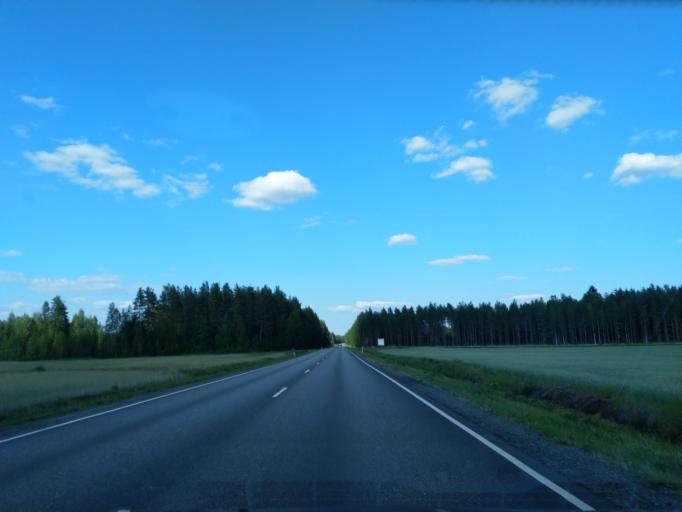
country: FI
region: Pirkanmaa
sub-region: Luoteis-Pirkanmaa
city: Kihnioe
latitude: 62.2100
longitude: 23.2413
